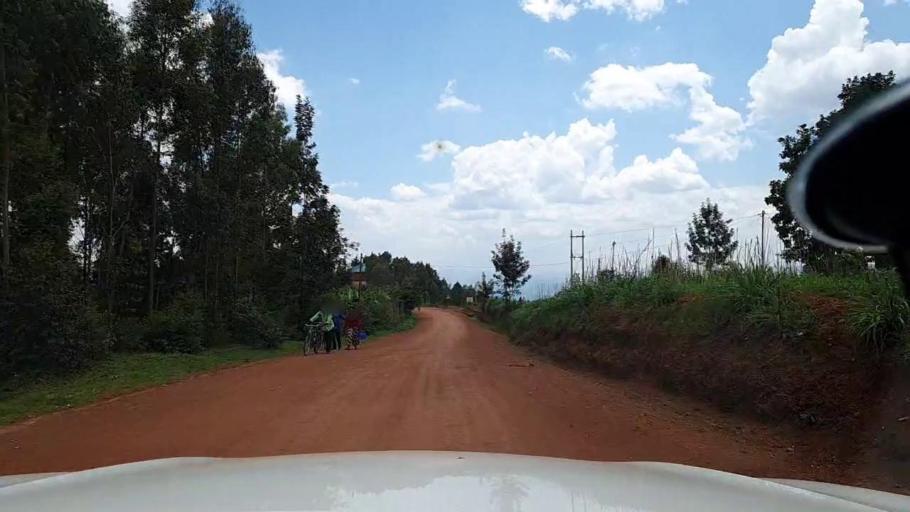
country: RW
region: Kigali
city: Kigali
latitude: -1.7968
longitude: 29.8446
